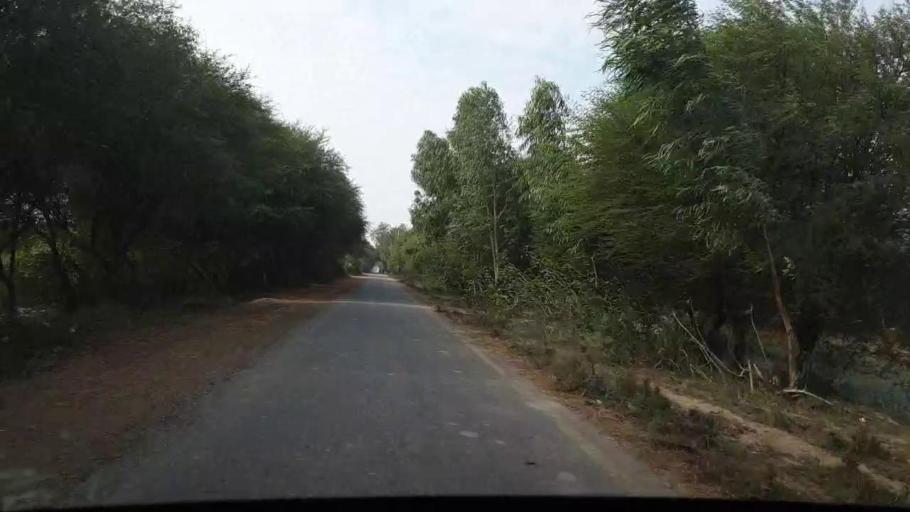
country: PK
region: Sindh
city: Chuhar Jamali
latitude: 24.3901
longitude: 67.9518
